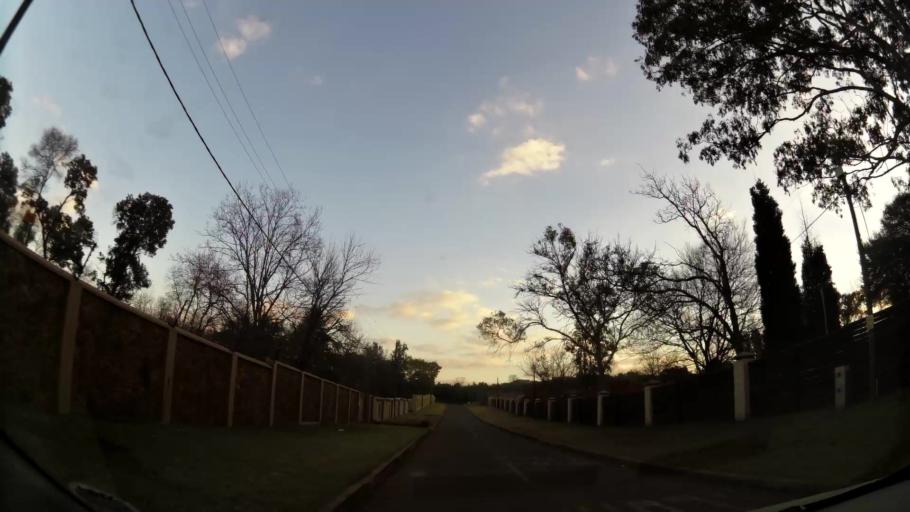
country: ZA
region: Gauteng
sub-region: West Rand District Municipality
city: Krugersdorp
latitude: -26.0681
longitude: 27.7985
